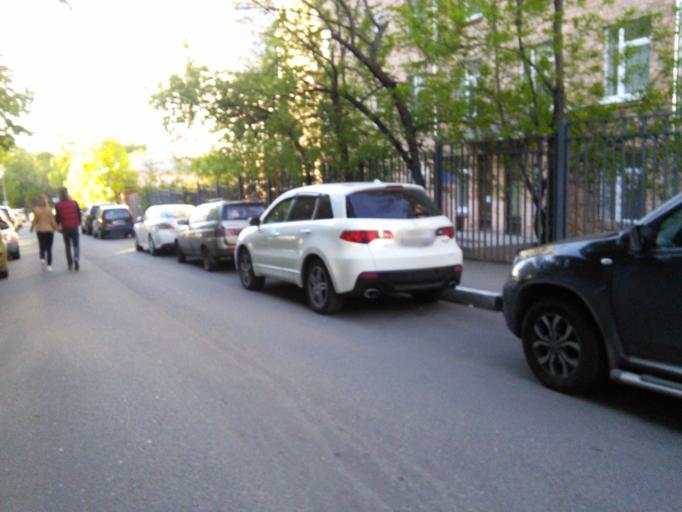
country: RU
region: Moskovskaya
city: Leninskiye Gory
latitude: 55.7014
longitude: 37.5626
